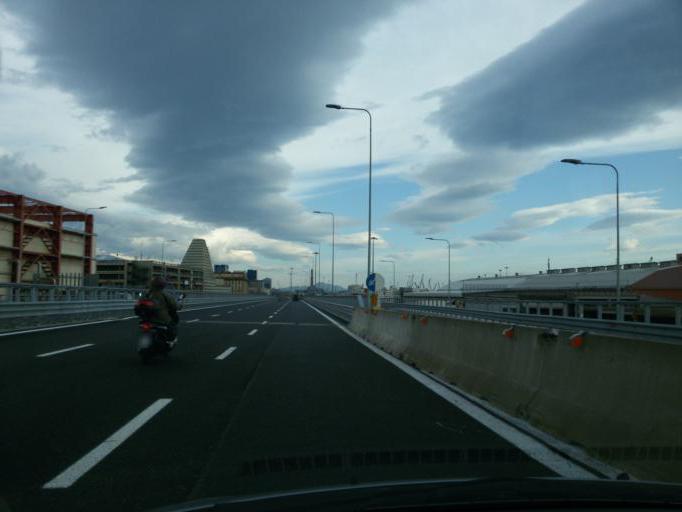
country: IT
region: Liguria
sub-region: Provincia di Genova
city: San Teodoro
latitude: 44.4120
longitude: 8.8781
